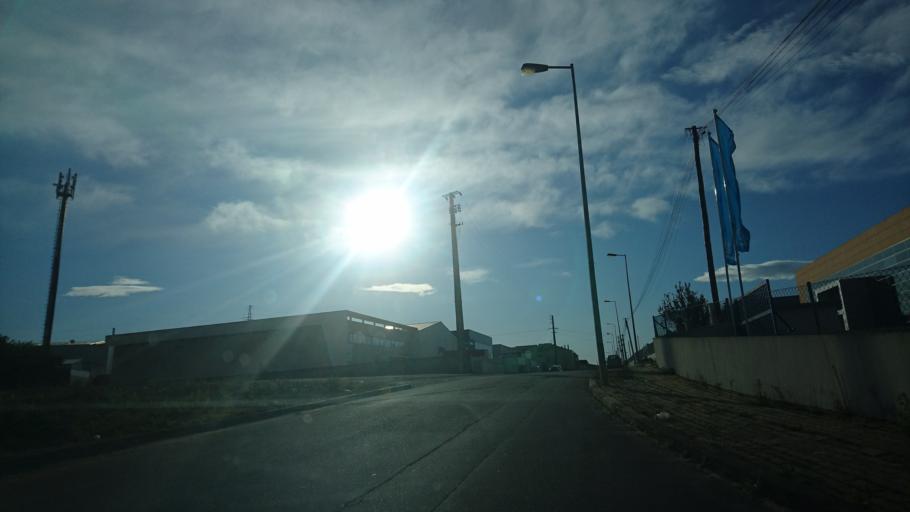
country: PT
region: Aveiro
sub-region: Santa Maria da Feira
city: Pacos de Brandao
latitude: 40.9632
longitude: -8.5981
